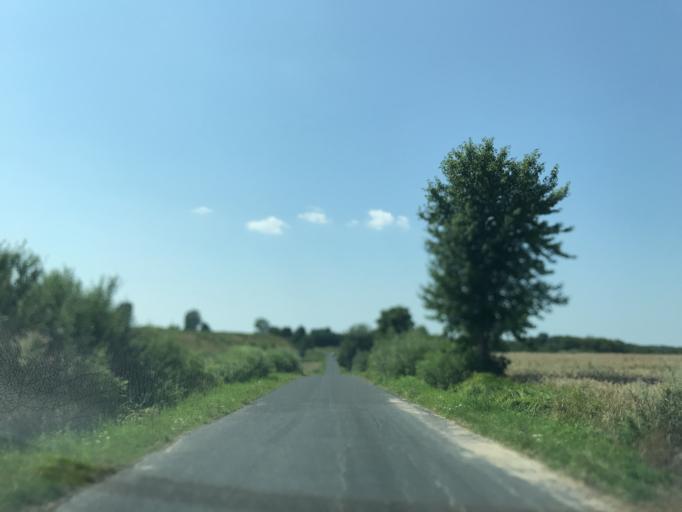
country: PL
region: Kujawsko-Pomorskie
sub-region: Powiat lipnowski
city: Chrostkowo
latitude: 52.9444
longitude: 19.2181
